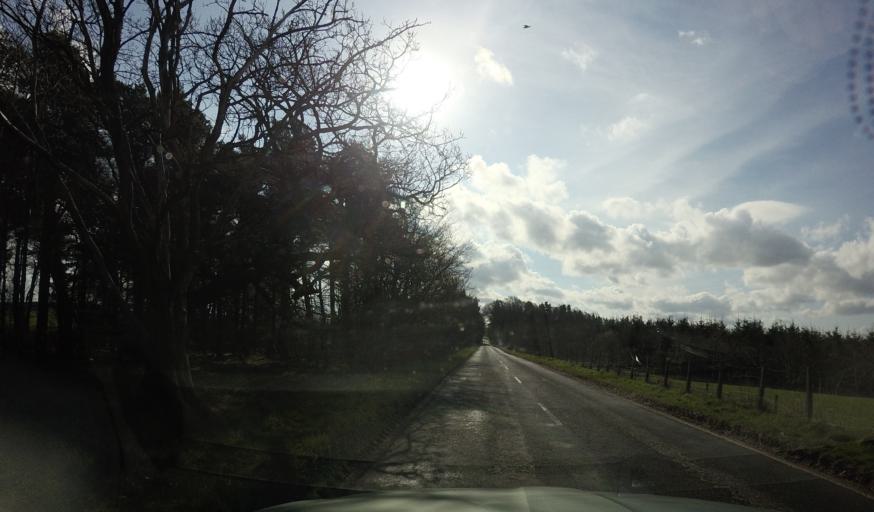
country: GB
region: Scotland
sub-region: Midlothian
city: Penicuik
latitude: 55.8158
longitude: -3.1977
